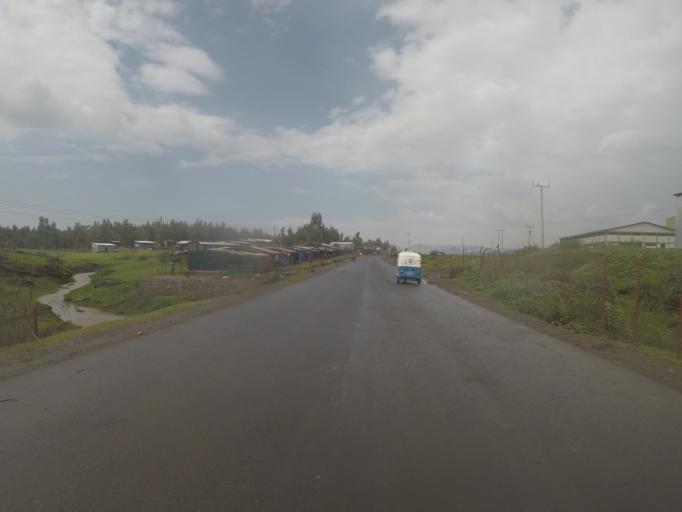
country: ET
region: Amhara
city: Debark'
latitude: 13.1232
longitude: 37.8839
